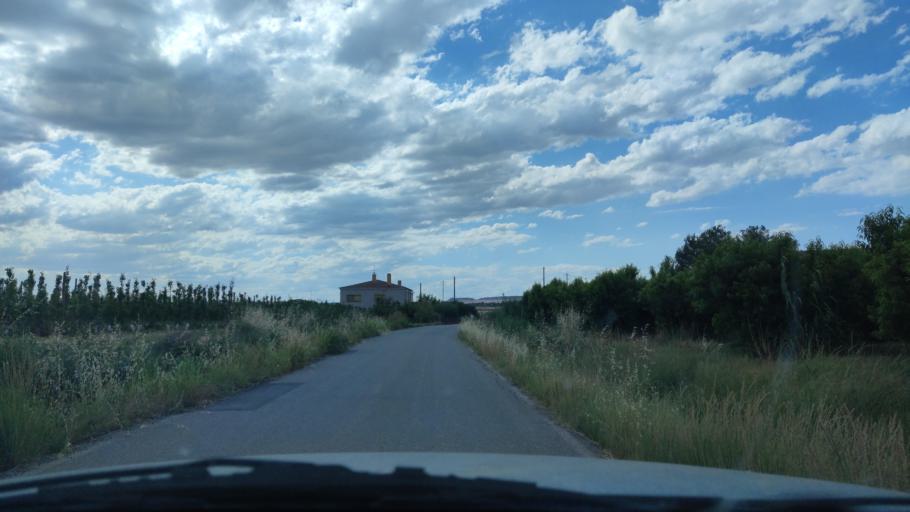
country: ES
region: Catalonia
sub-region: Provincia de Lleida
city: Lleida
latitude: 41.5967
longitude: 0.5700
